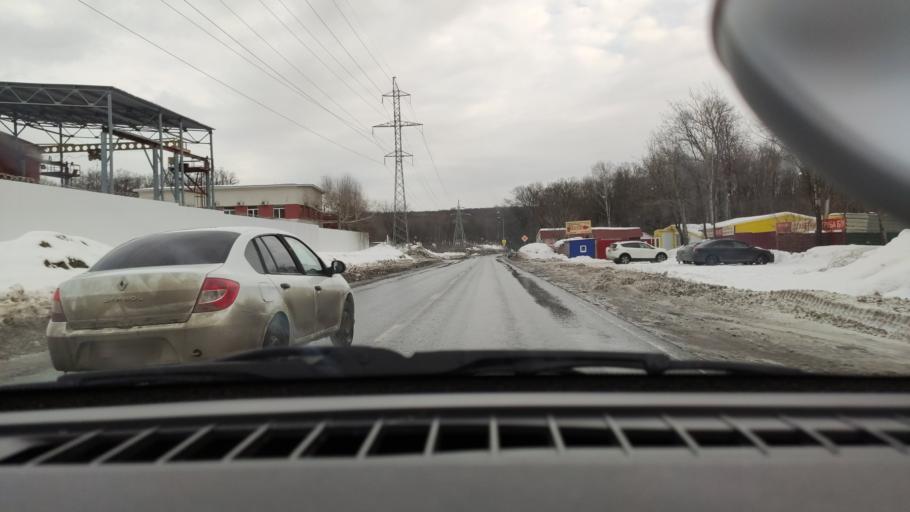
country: RU
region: Samara
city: Novosemeykino
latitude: 53.3478
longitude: 50.2368
